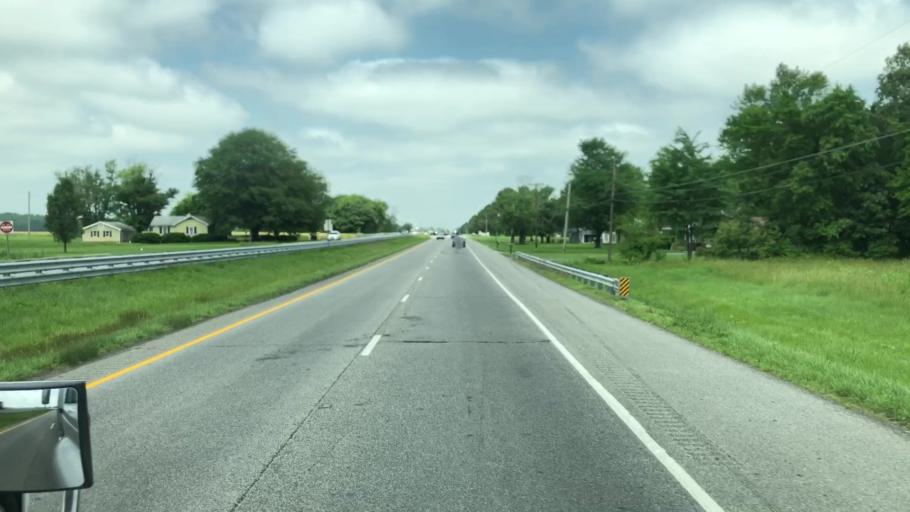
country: US
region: Maryland
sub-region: Talbot County
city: Easton
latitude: 38.8168
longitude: -76.0599
